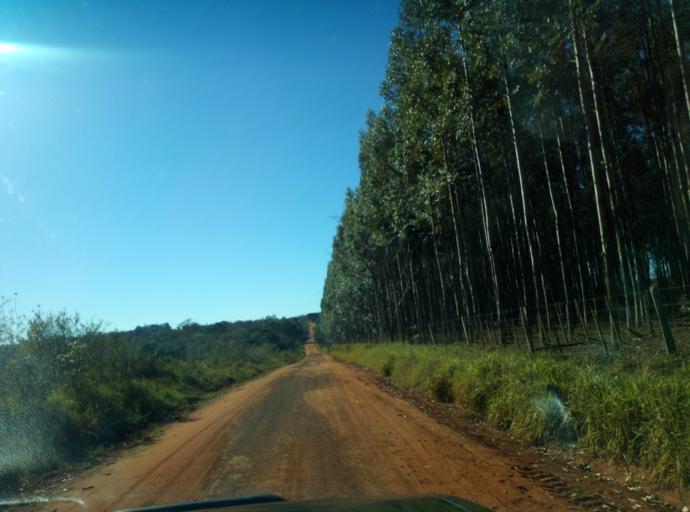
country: PY
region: Caaguazu
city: Doctor Cecilio Baez
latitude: -25.1632
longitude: -56.2616
